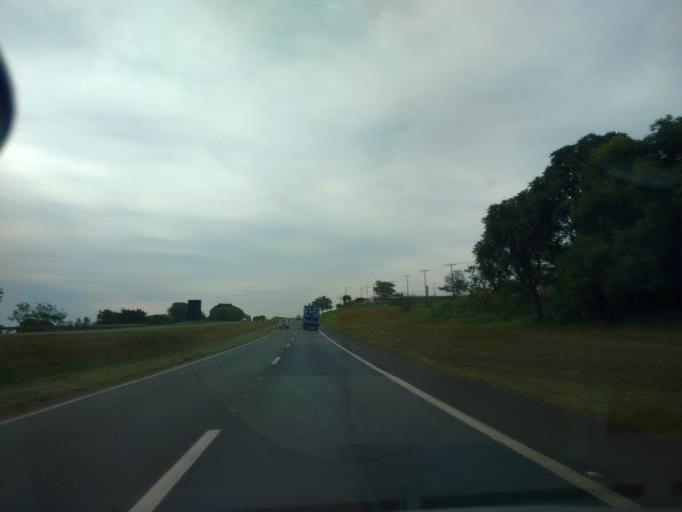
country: BR
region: Sao Paulo
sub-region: Araraquara
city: Araraquara
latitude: -21.7983
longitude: -48.2061
